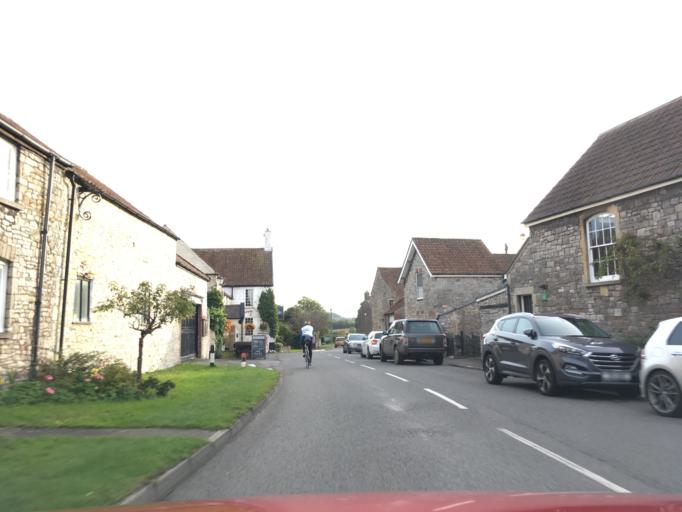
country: GB
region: England
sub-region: South Gloucestershire
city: Almondsbury
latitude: 51.5763
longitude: -2.5657
